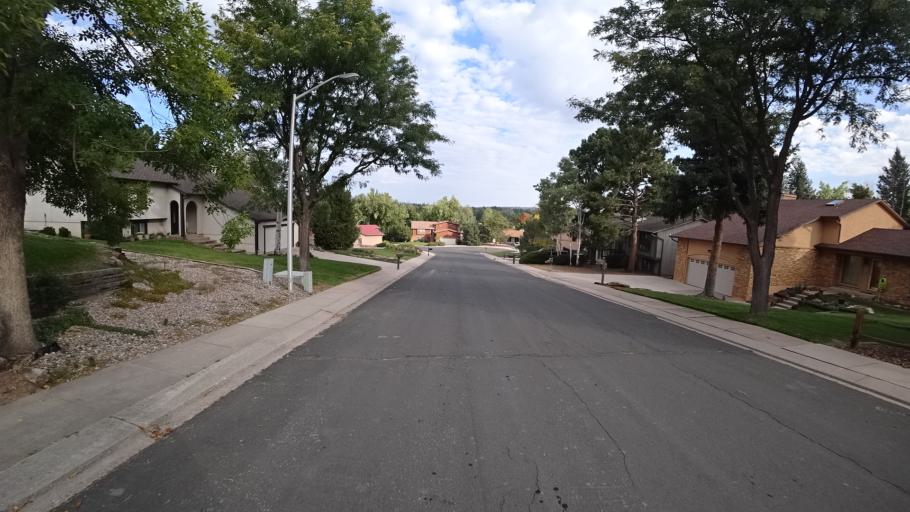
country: US
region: Colorado
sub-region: El Paso County
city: Cimarron Hills
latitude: 38.8694
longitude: -104.7495
